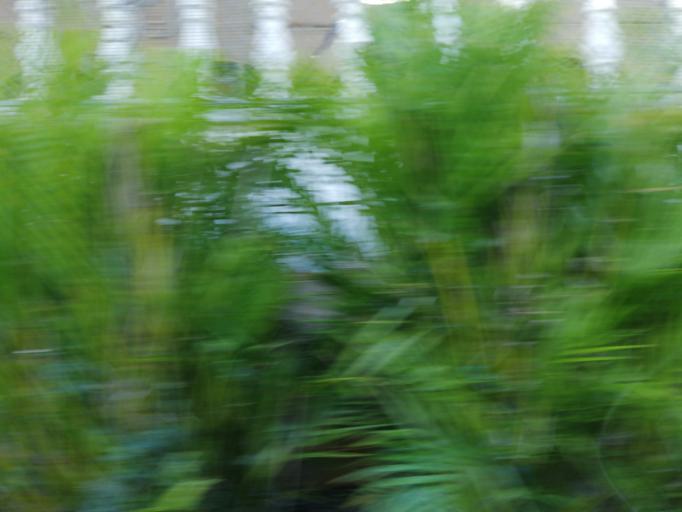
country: MU
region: Moka
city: Moka
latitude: -20.2223
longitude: 57.4716
